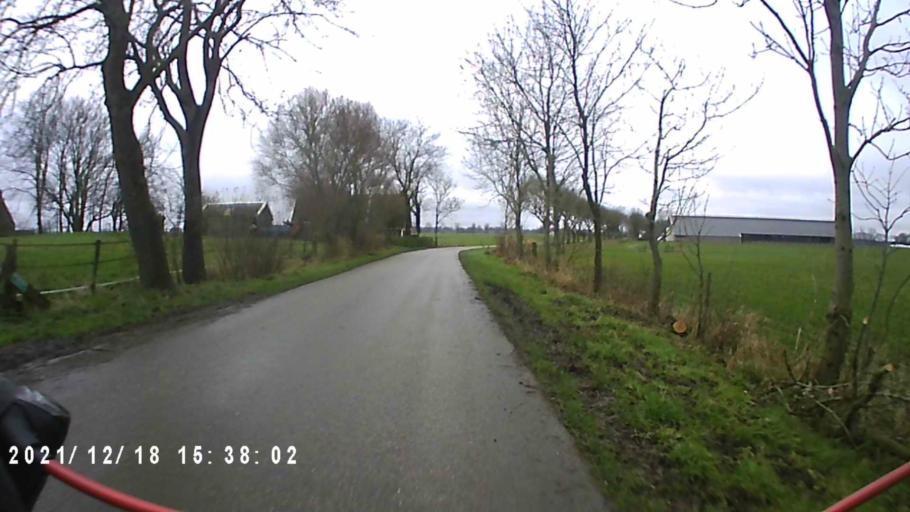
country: NL
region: Friesland
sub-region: Gemeente Dongeradeel
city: Anjum
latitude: 53.3387
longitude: 6.1218
